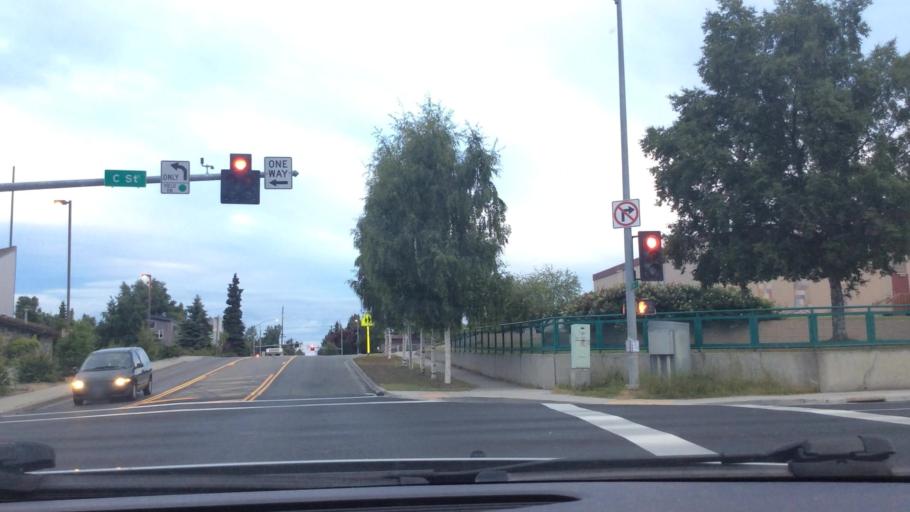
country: US
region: Alaska
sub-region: Anchorage Municipality
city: Anchorage
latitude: 61.2077
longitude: -149.8871
